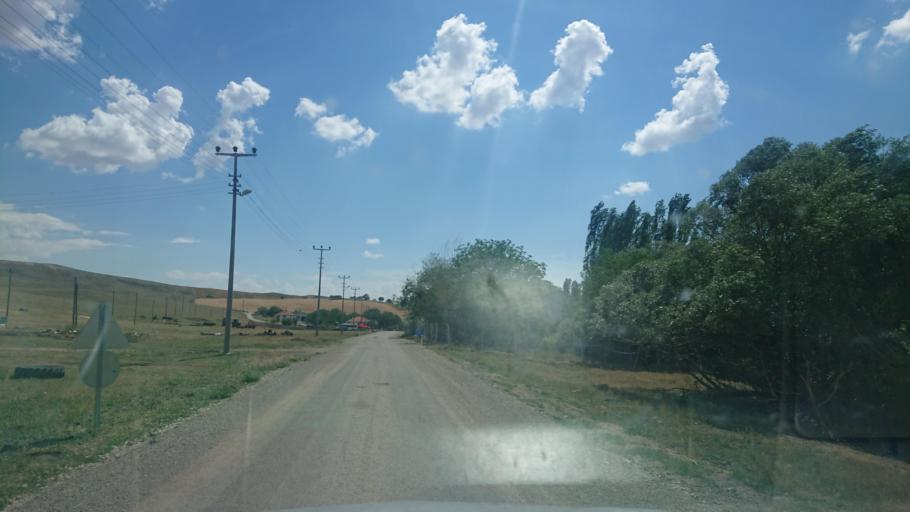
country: TR
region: Aksaray
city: Agacoren
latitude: 38.8393
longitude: 33.8143
